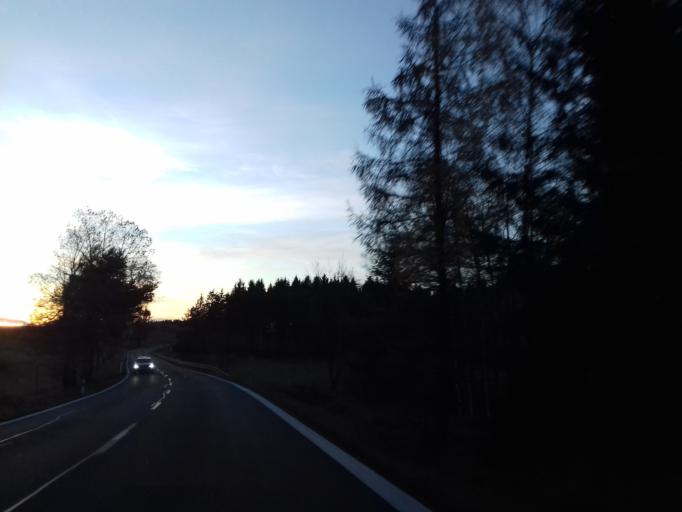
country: CZ
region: Vysocina
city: Krizova
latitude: 49.6756
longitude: 15.7592
